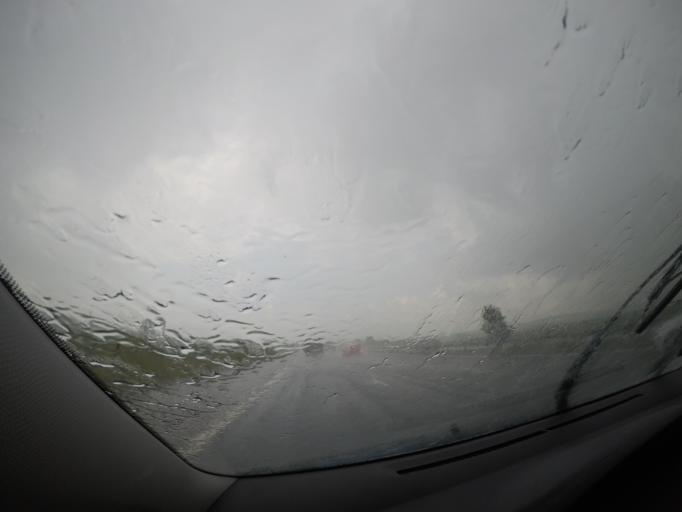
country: GB
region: England
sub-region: Cumbria
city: Penrith
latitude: 54.7065
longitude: -2.7928
